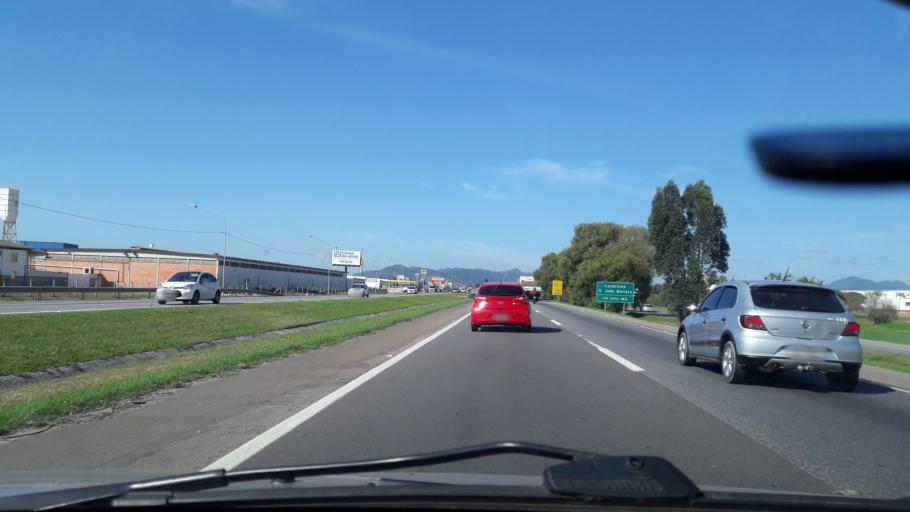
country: BR
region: Santa Catarina
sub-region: Tijucas
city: Tijucas
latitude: -27.2257
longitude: -48.6279
